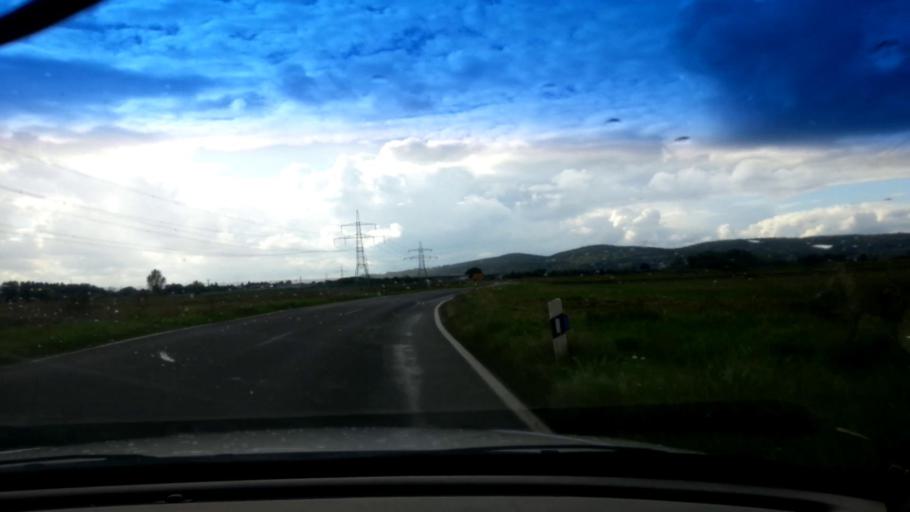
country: DE
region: Bavaria
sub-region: Upper Franconia
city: Hallstadt
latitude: 49.9357
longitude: 10.8961
